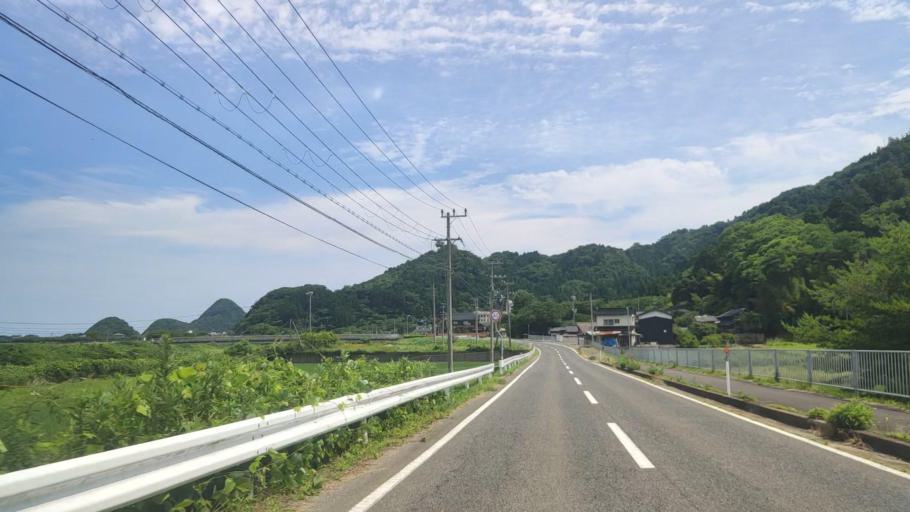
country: JP
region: Hyogo
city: Toyooka
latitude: 35.6462
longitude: 134.7629
